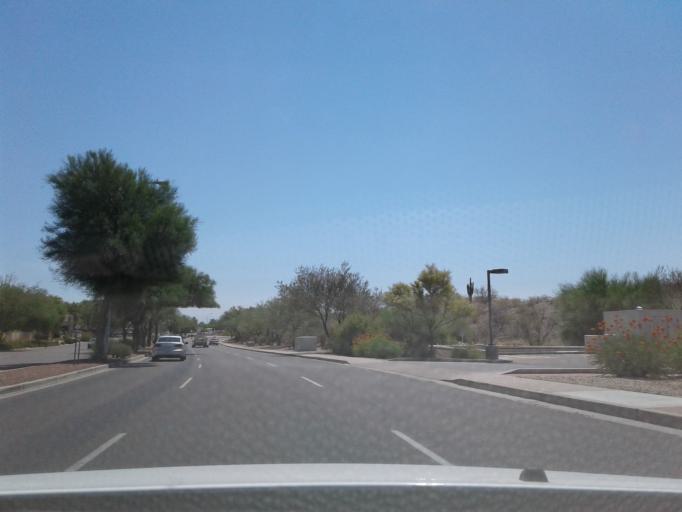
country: US
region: Arizona
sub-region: Maricopa County
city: Guadalupe
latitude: 33.3198
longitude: -111.9919
